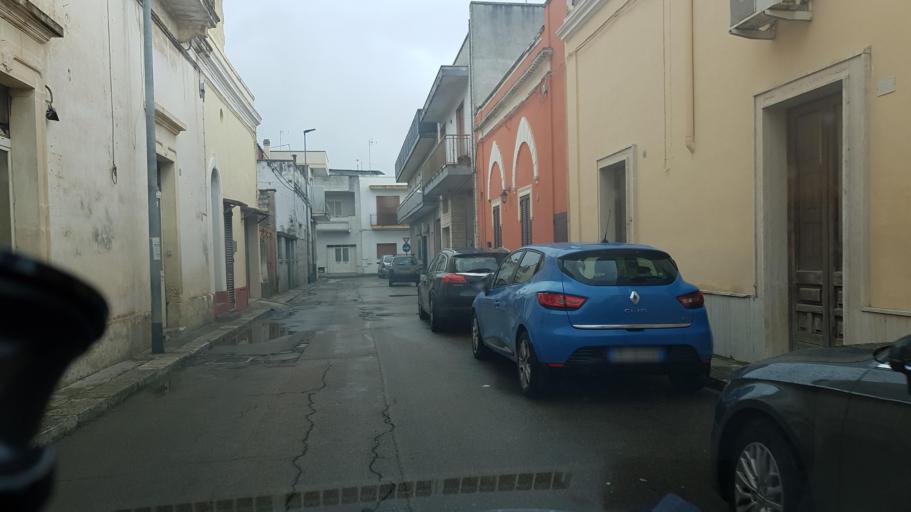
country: IT
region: Apulia
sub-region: Provincia di Lecce
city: Carmiano
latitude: 40.3484
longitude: 18.0451
